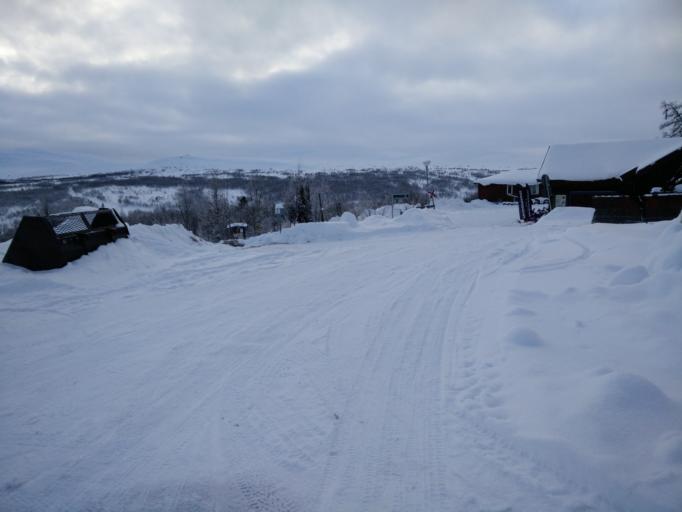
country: NO
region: Sor-Trondelag
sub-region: Tydal
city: Aas
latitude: 62.6502
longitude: 12.3960
